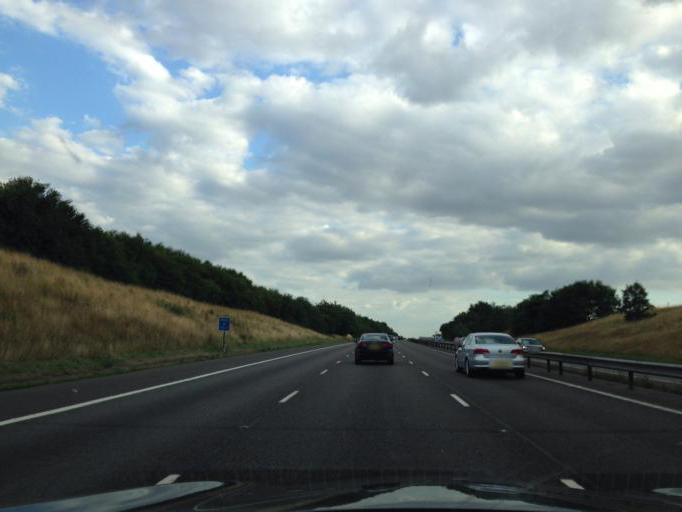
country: GB
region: England
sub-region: Oxfordshire
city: Somerton
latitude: 51.9975
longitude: -1.2687
